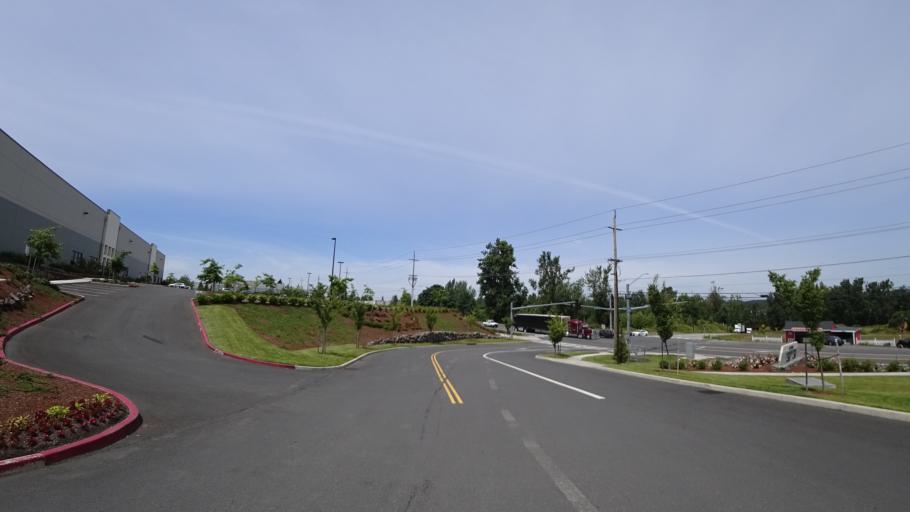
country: US
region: Oregon
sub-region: Multnomah County
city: Fairview
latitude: 45.5452
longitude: -122.4718
